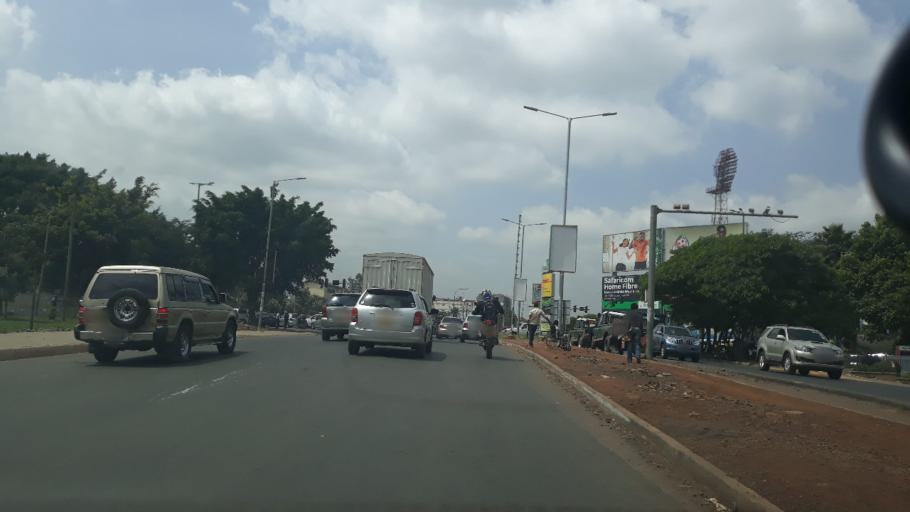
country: KE
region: Nairobi Area
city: Nairobi
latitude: -1.3045
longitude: 36.8274
